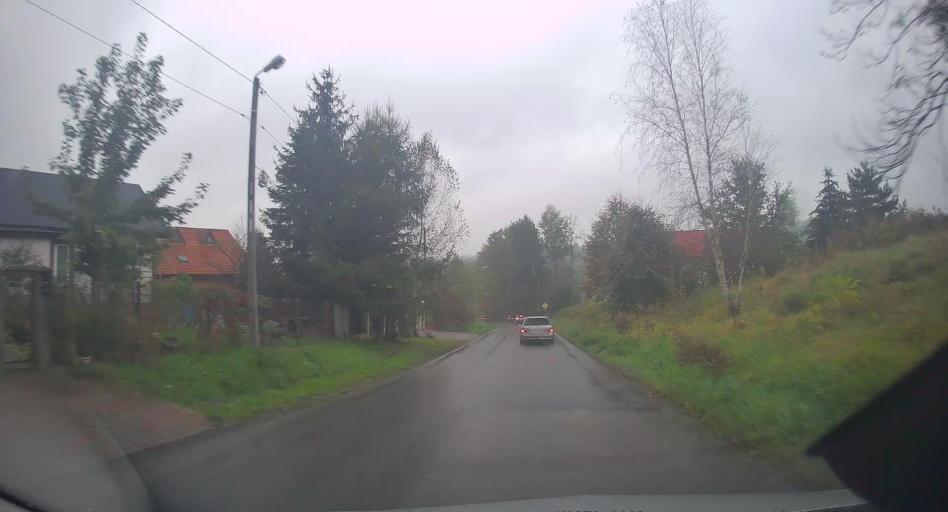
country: PL
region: Lesser Poland Voivodeship
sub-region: Powiat krakowski
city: Ochojno
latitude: 49.9673
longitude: 19.9987
